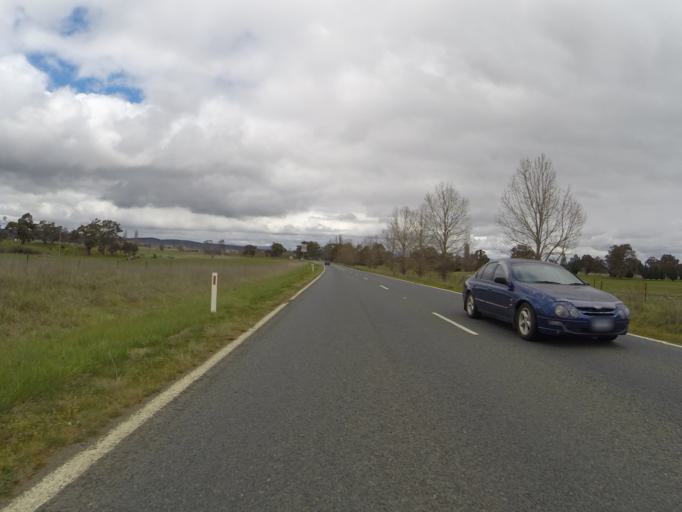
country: AU
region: Australian Capital Territory
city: Canberra
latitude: -35.2565
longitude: 149.1905
